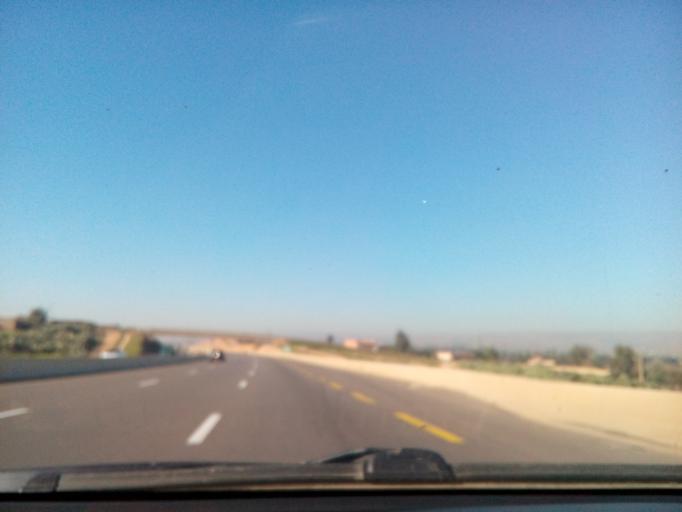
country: DZ
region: Chlef
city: Boukadir
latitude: 36.0500
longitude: 1.1188
